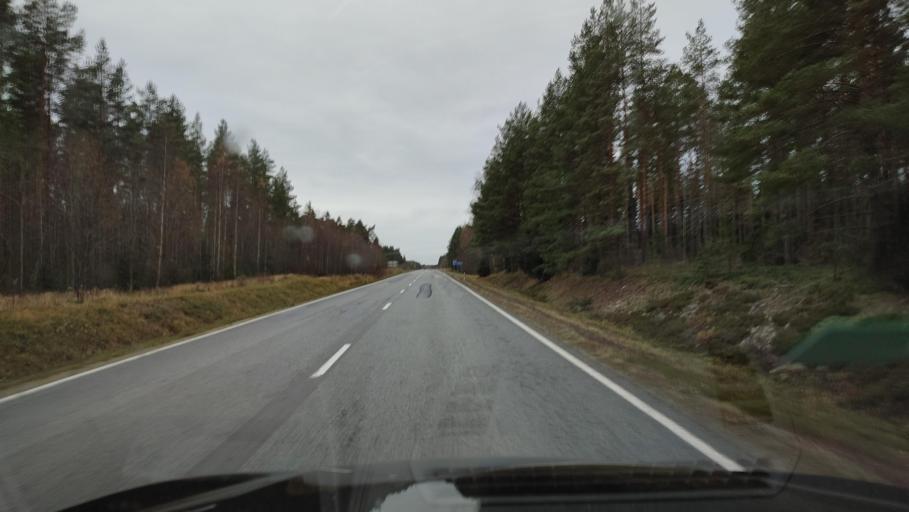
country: FI
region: Ostrobothnia
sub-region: Sydosterbotten
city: Naerpes
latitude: 62.4007
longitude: 21.3730
